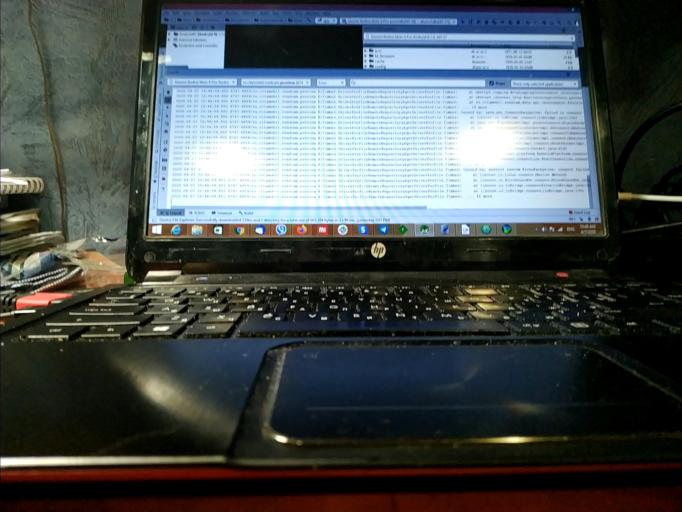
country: RU
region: Vologda
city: Suda
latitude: 58.9229
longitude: 37.5432
